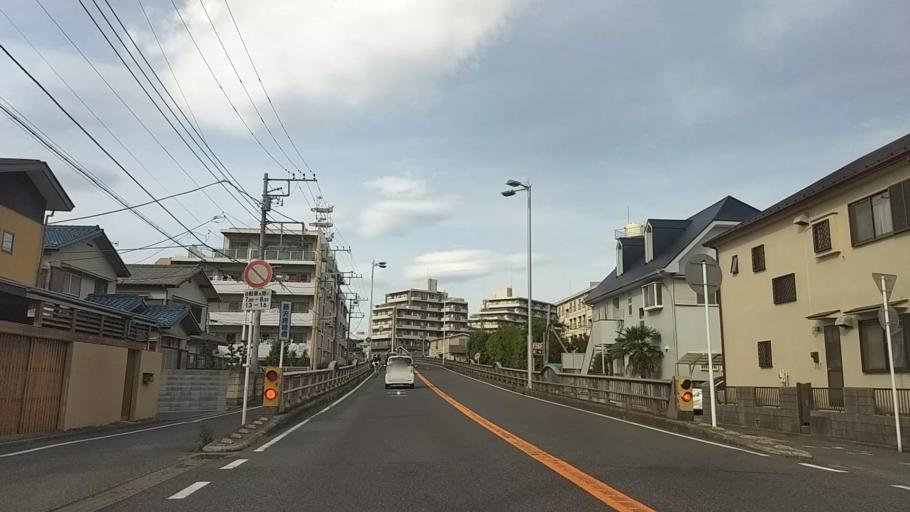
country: JP
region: Kanagawa
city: Fujisawa
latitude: 35.3367
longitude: 139.4750
